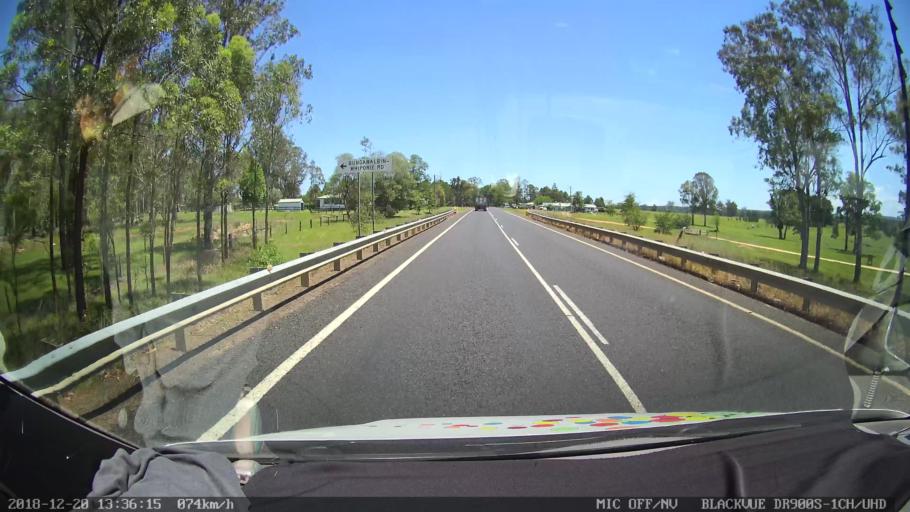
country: AU
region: New South Wales
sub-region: Clarence Valley
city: Maclean
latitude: -29.2798
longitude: 152.9904
